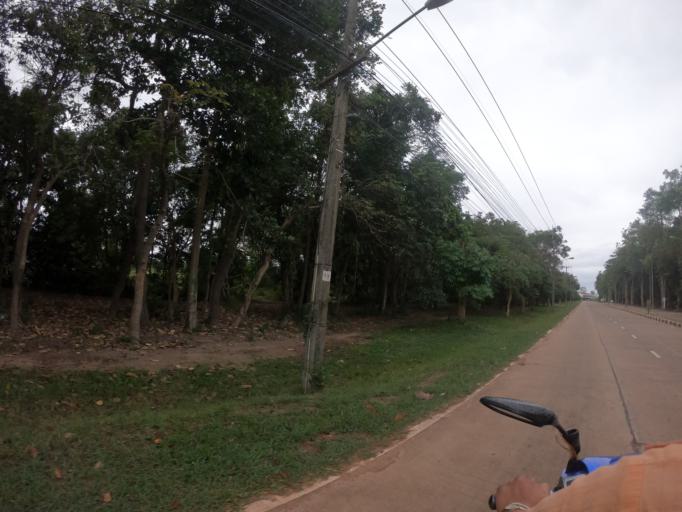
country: TH
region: Roi Et
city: Chiang Khwan
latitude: 16.1455
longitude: 103.8721
